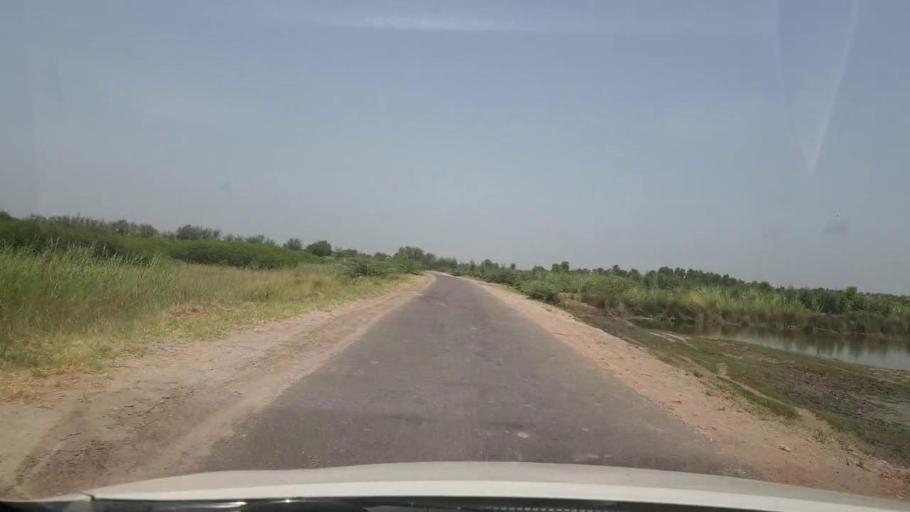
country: PK
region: Sindh
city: Bozdar
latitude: 27.2551
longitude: 68.6387
